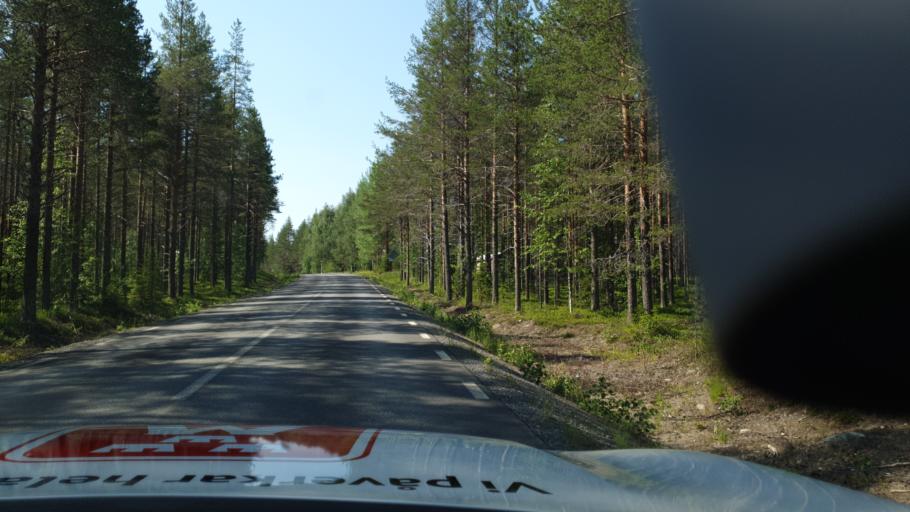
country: SE
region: Vaesterbotten
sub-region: Skelleftea Kommun
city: Langsele
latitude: 64.9764
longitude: 20.0549
